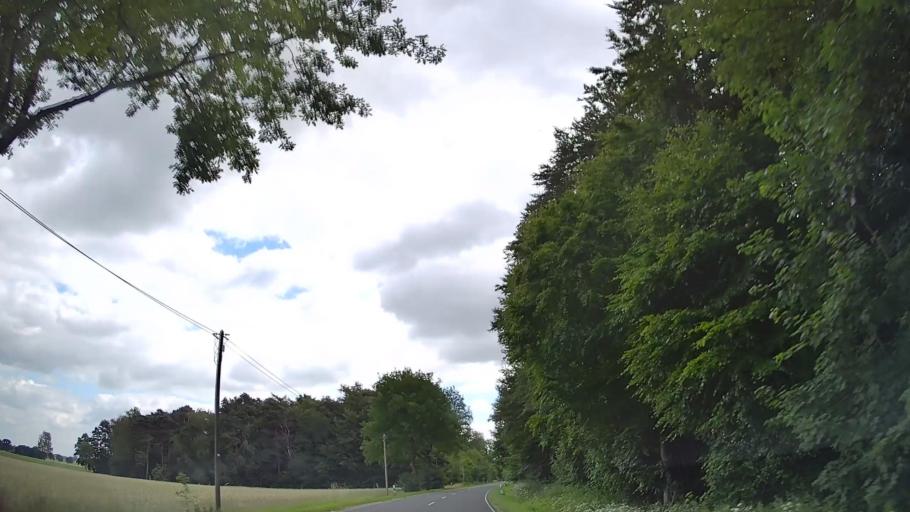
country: DE
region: Lower Saxony
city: Brockum
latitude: 52.4640
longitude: 8.4573
